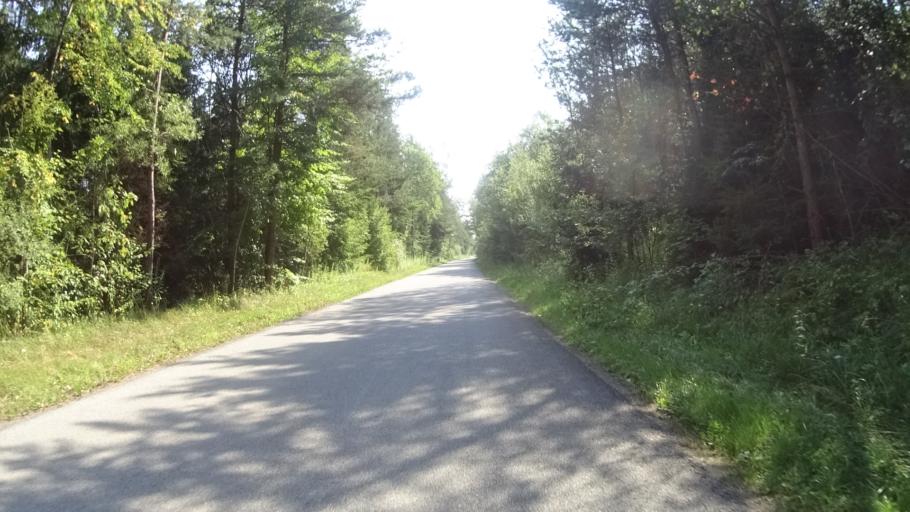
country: AT
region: Carinthia
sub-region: Politischer Bezirk Klagenfurt Land
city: Grafenstein
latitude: 46.5591
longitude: 14.4202
